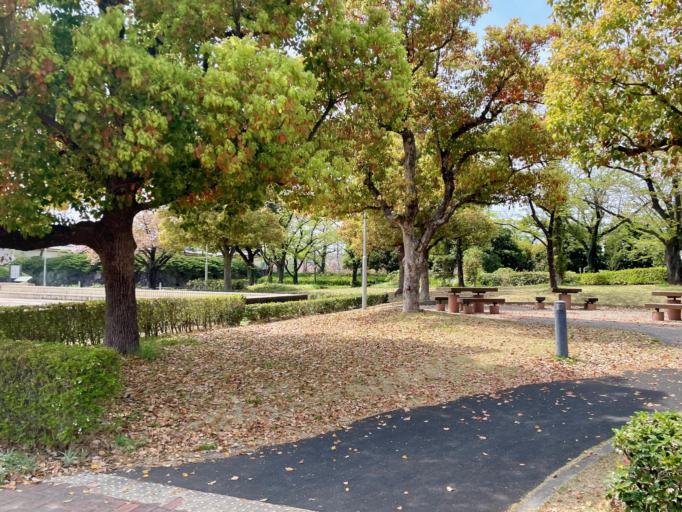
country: JP
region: Saitama
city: Fukayacho
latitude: 36.1991
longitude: 139.2862
